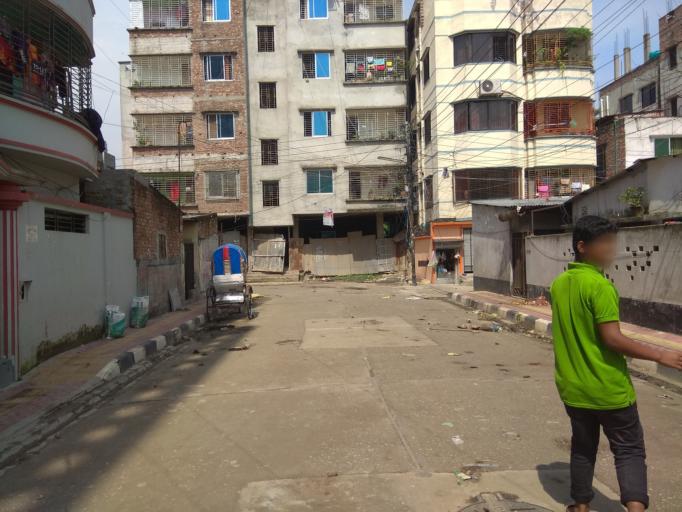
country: BD
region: Dhaka
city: Azimpur
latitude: 23.8086
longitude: 90.3541
